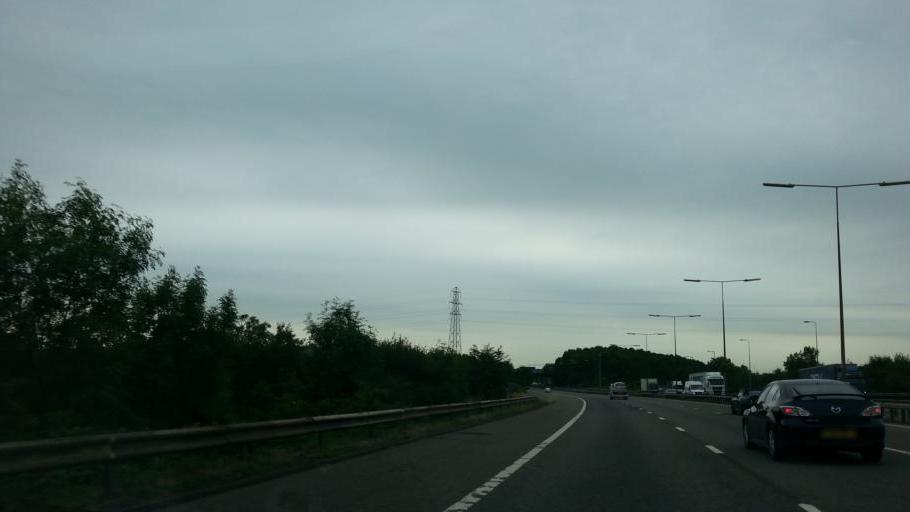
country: GB
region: England
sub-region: Warwickshire
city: Bedworth
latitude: 52.4457
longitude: -1.4252
